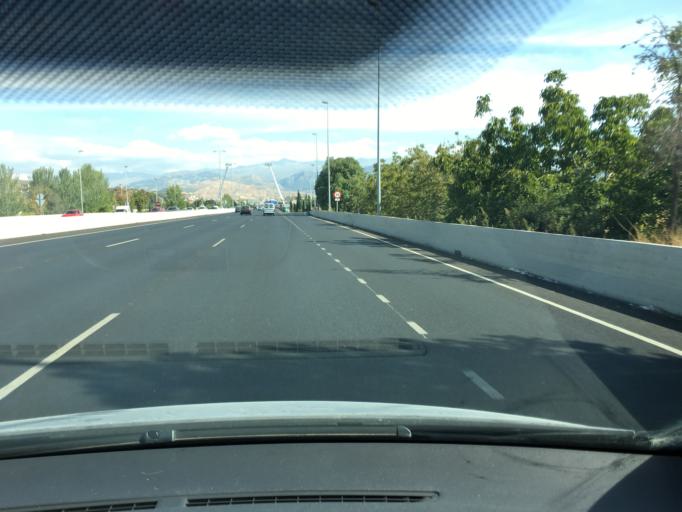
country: ES
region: Andalusia
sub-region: Provincia de Granada
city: Granada
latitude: 37.1840
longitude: -3.6277
